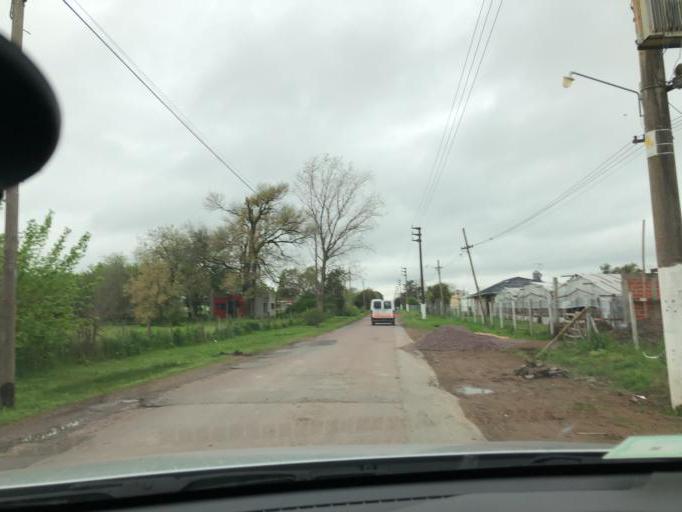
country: AR
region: Buenos Aires
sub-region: Partido de La Plata
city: La Plata
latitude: -34.8995
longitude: -58.0908
